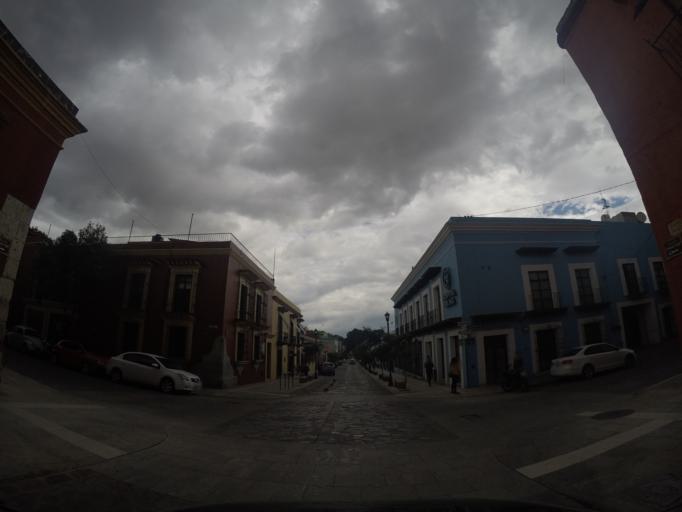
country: MX
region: Oaxaca
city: Oaxaca de Juarez
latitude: 17.0650
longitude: -96.7250
